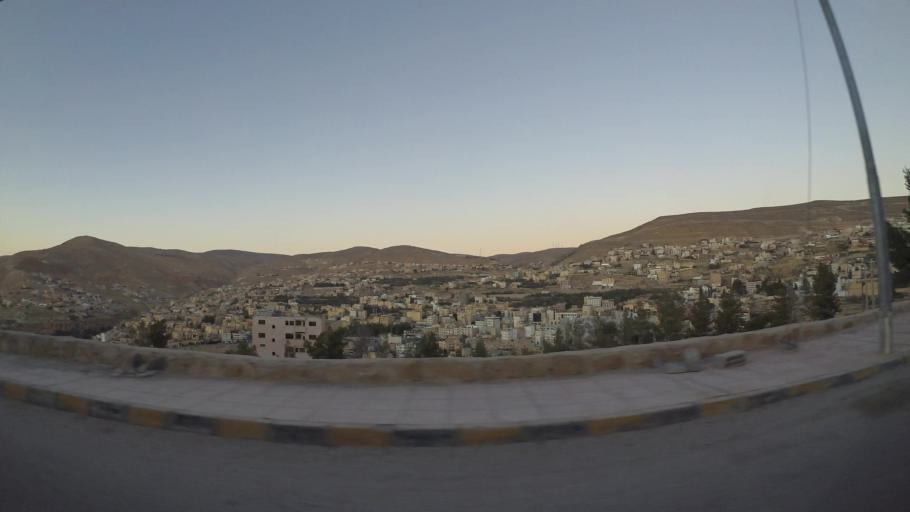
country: JO
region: Ma'an
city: Petra
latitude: 30.3185
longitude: 35.4747
